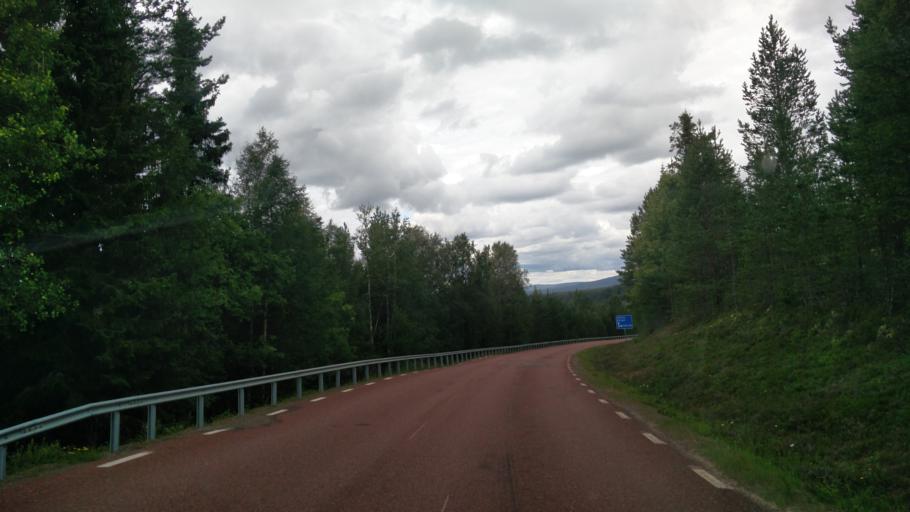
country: NO
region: Hedmark
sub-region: Trysil
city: Innbygda
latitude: 61.1474
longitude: 12.8020
